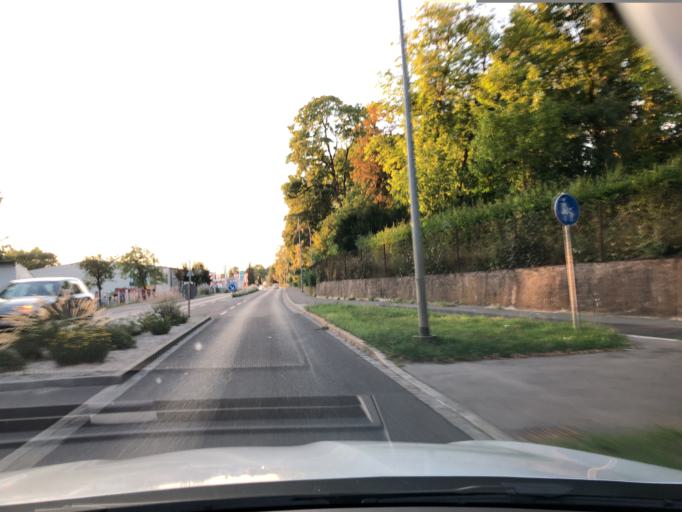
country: DE
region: Bavaria
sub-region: Upper Palatinate
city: Sulzbach-Rosenberg
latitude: 49.4946
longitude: 11.7572
